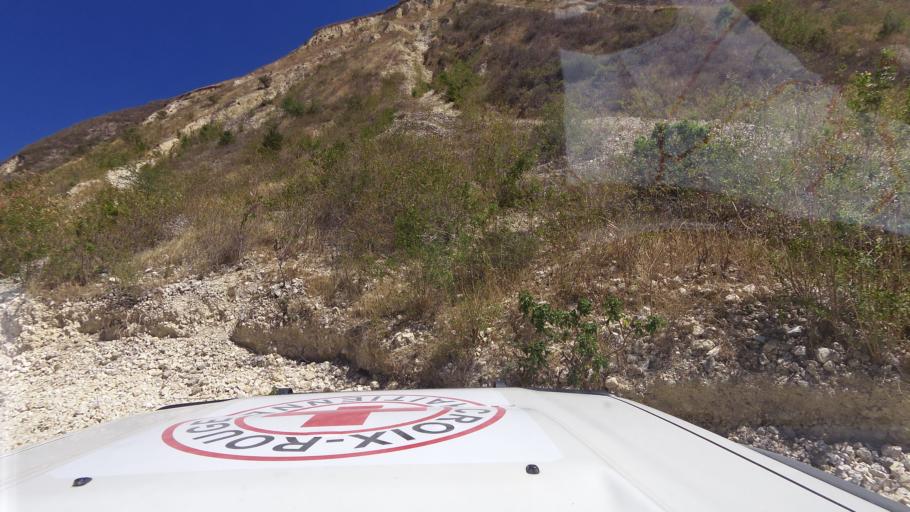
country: HT
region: Ouest
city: Croix des Bouquets
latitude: 18.6836
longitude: -72.2854
